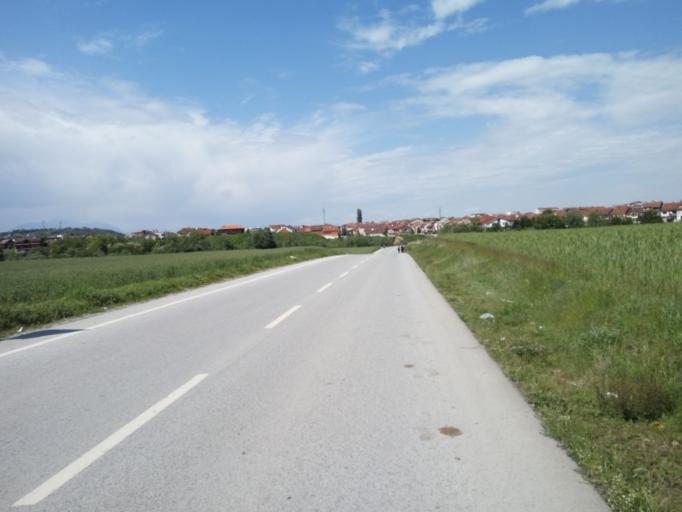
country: XK
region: Gjakova
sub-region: Komuna e Gjakoves
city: Gjakove
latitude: 42.3629
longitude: 20.4355
